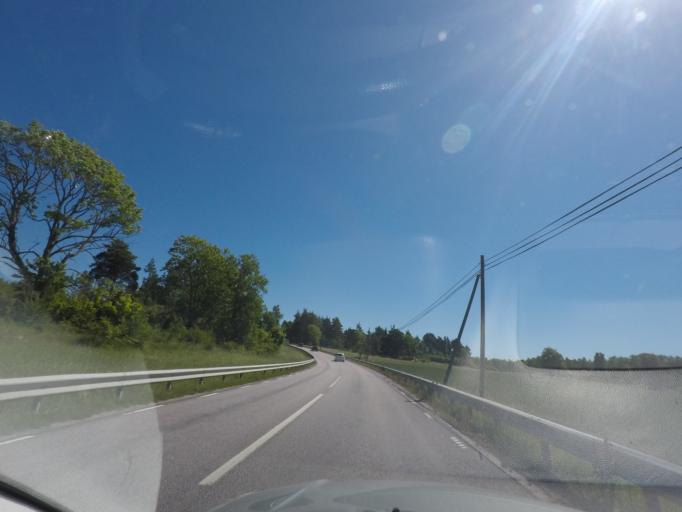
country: SE
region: Stockholm
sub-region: Sigtuna Kommun
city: Sigtuna
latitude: 59.6563
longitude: 17.6927
